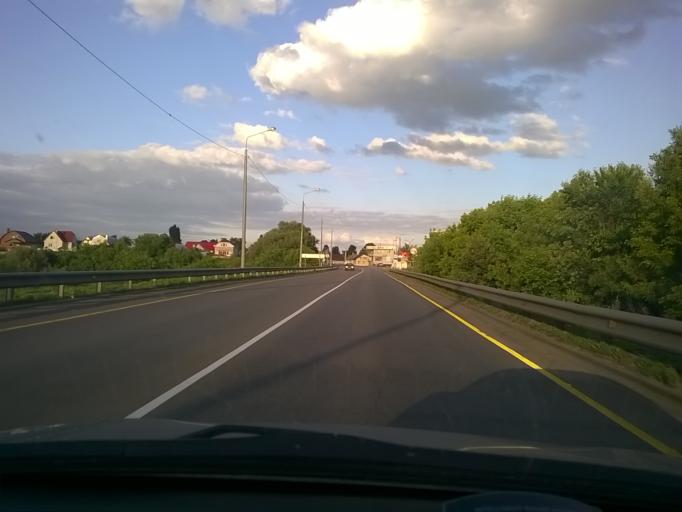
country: RU
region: Voronezj
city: Borisoglebsk
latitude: 51.3754
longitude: 42.0566
